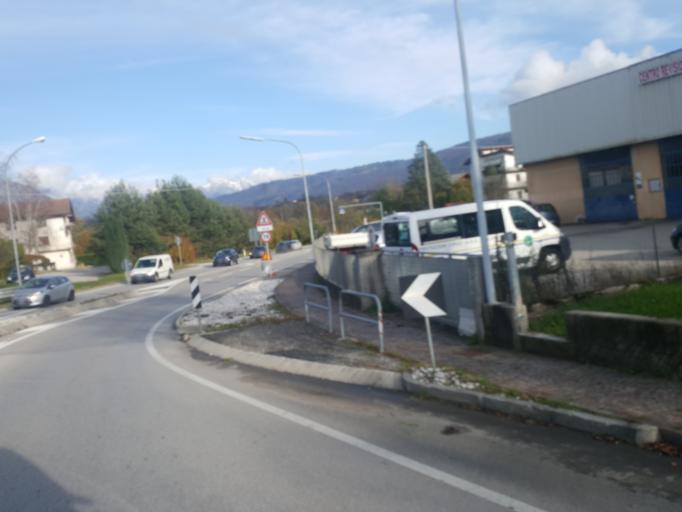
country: IT
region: Veneto
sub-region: Provincia di Belluno
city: Limana
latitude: 46.1069
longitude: 12.1928
